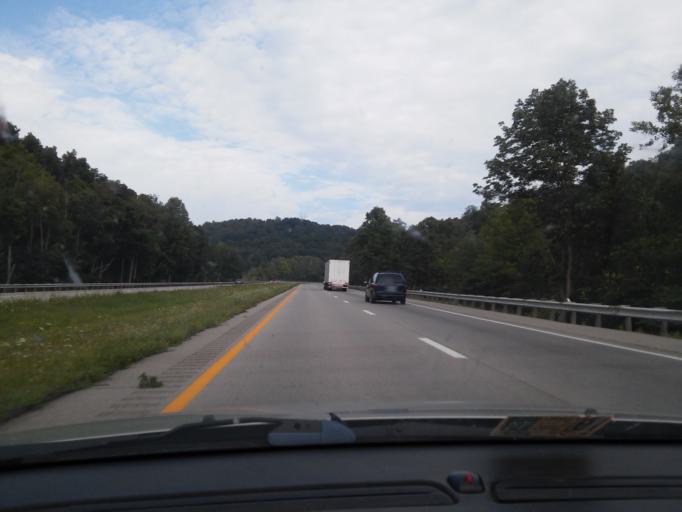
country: US
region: Ohio
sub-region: Pike County
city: Waverly
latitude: 39.1958
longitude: -82.7954
